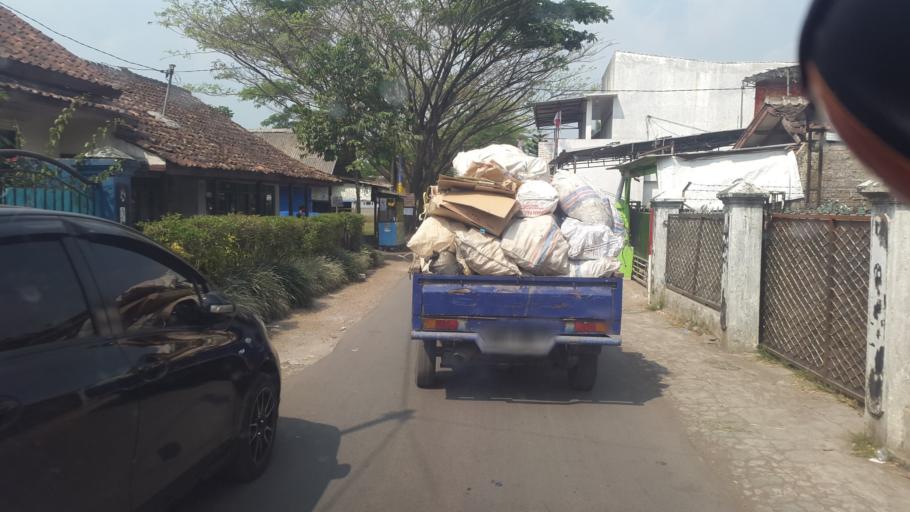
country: ID
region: West Java
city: Sukabumi
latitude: -6.9490
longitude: 106.9687
